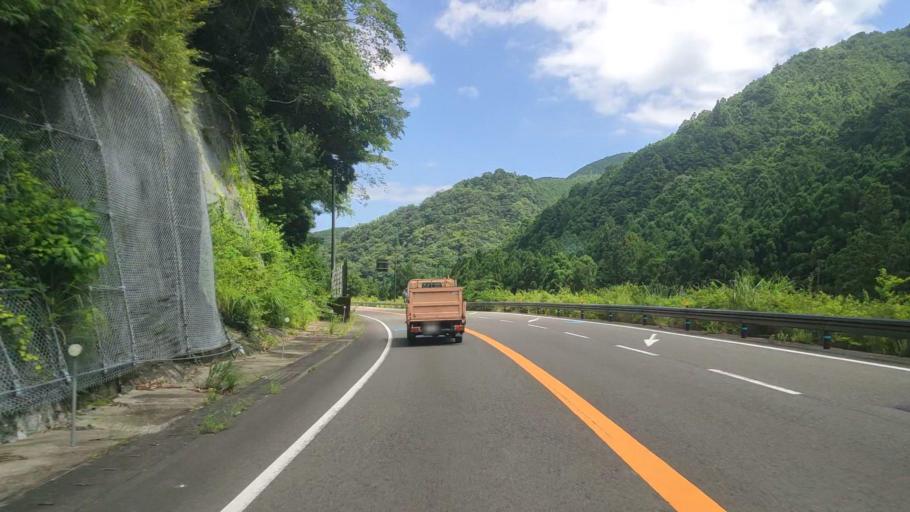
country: JP
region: Mie
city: Owase
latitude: 33.9243
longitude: 136.0935
